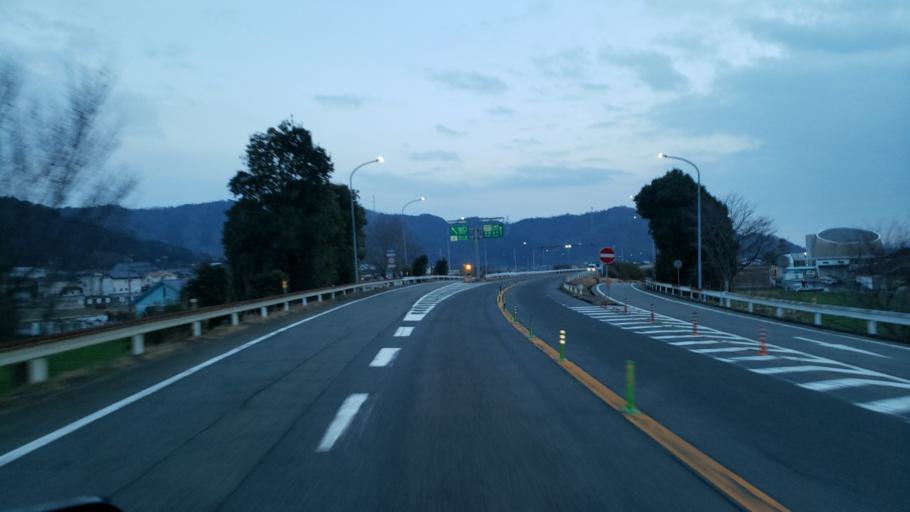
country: JP
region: Hyogo
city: Himeji
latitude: 34.9870
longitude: 134.7701
